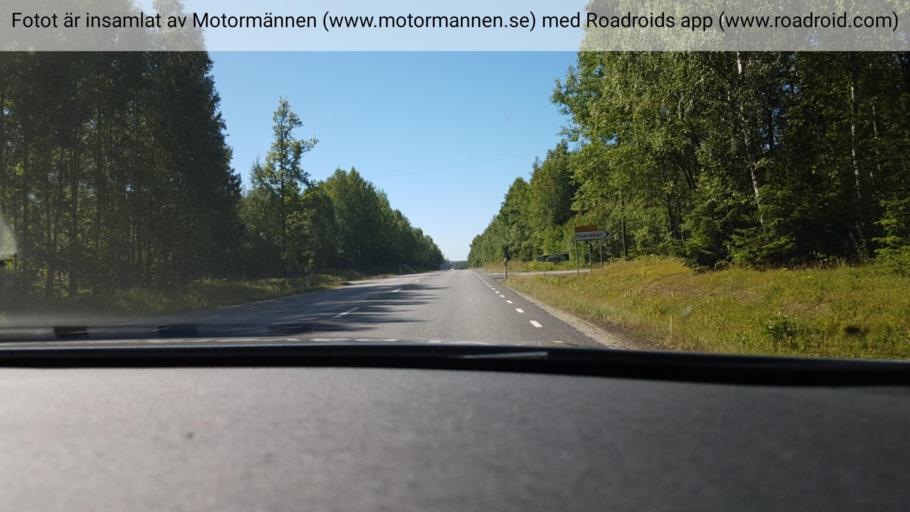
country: SE
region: Joenkoeping
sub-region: Habo Kommun
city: Habo
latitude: 57.9768
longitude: 14.1053
